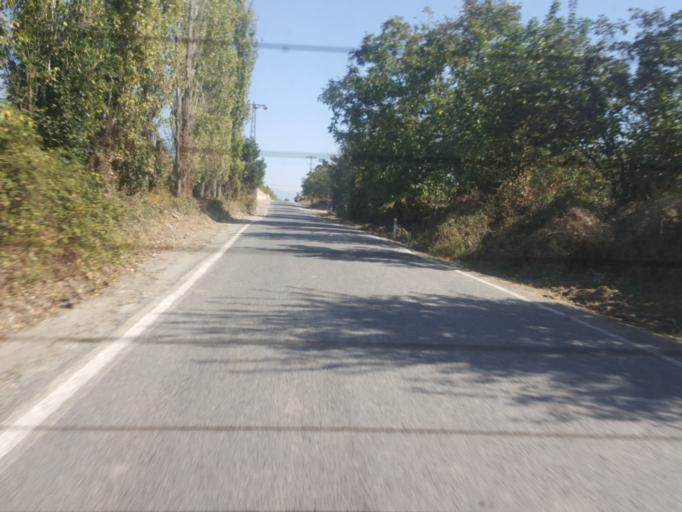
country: TR
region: Kastamonu
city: Tosya
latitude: 40.9893
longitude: 34.1110
